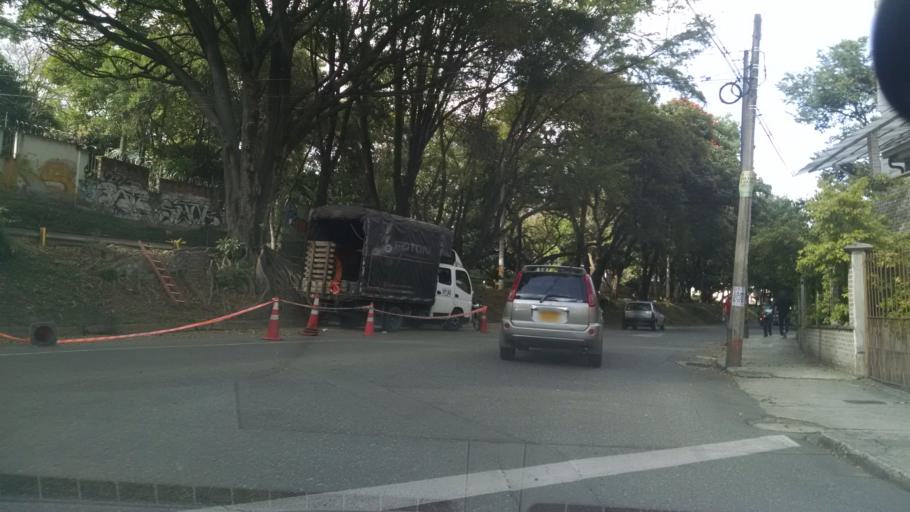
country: CO
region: Antioquia
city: Medellin
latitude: 6.2631
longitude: -75.6009
